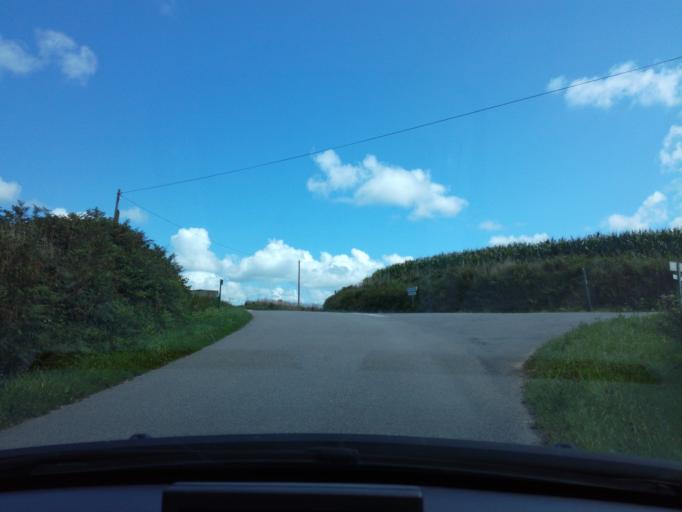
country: FR
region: Brittany
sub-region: Departement du Finistere
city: Saint-Pabu
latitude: 48.5508
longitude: -4.6006
